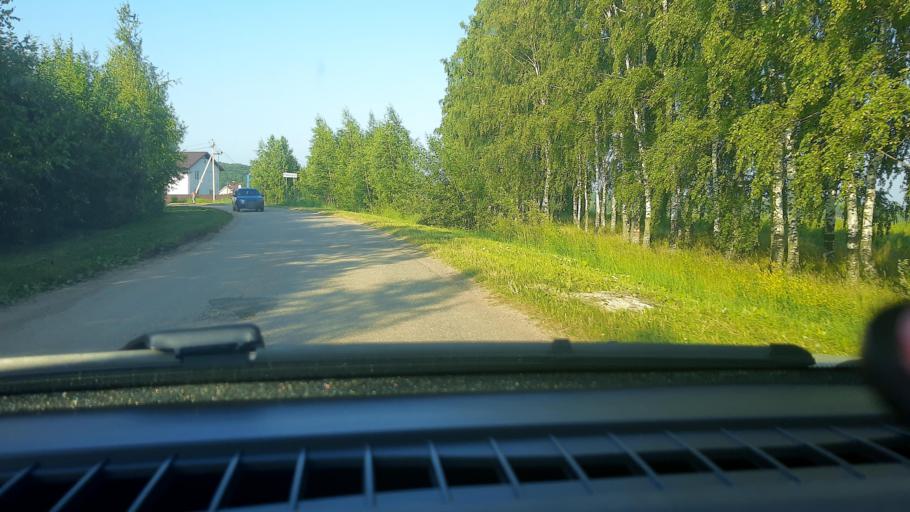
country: RU
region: Nizjnij Novgorod
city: Nizhniy Novgorod
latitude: 56.1951
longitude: 43.9562
